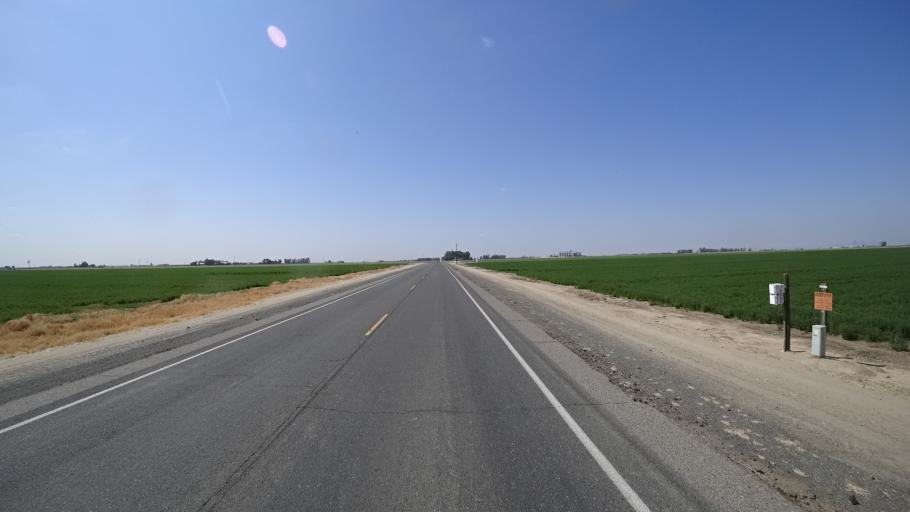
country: US
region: California
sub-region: Kings County
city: Home Garden
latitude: 36.2354
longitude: -119.6369
